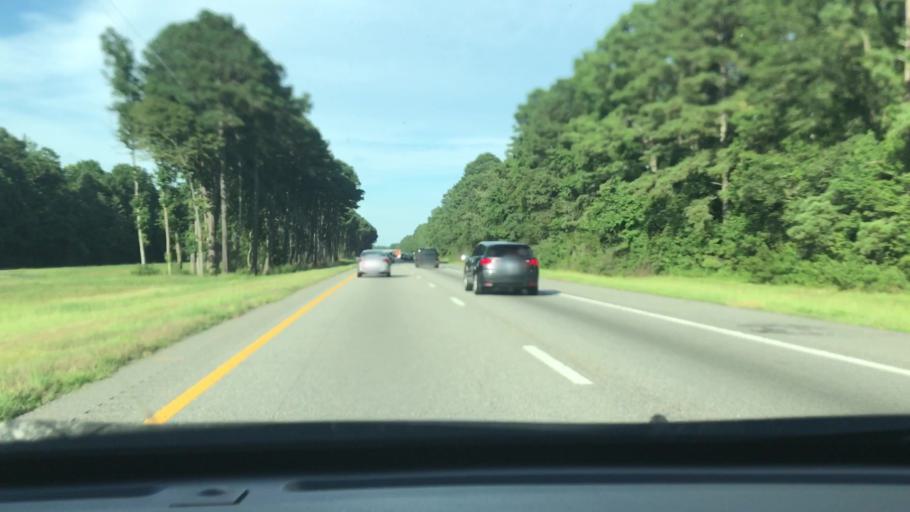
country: US
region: North Carolina
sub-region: Robeson County
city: Rowland
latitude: 34.5454
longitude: -79.2179
